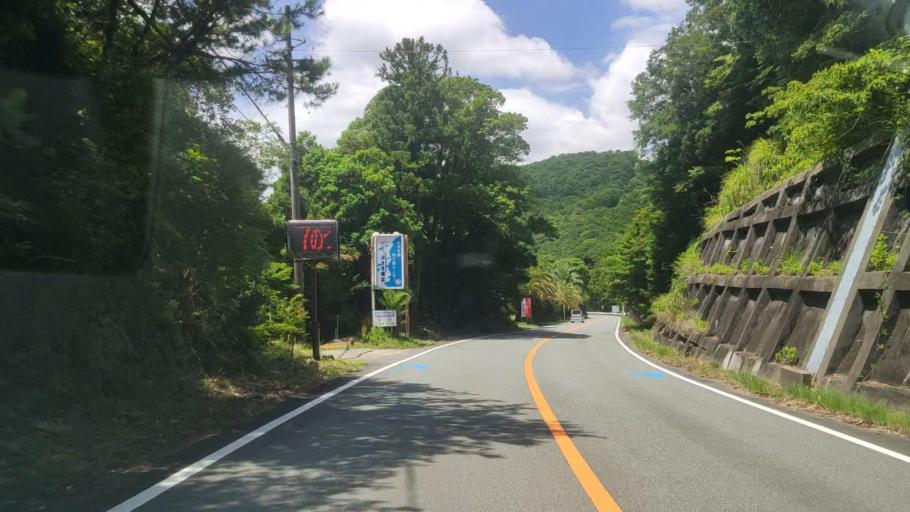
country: JP
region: Mie
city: Ise
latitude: 34.3171
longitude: 136.6470
